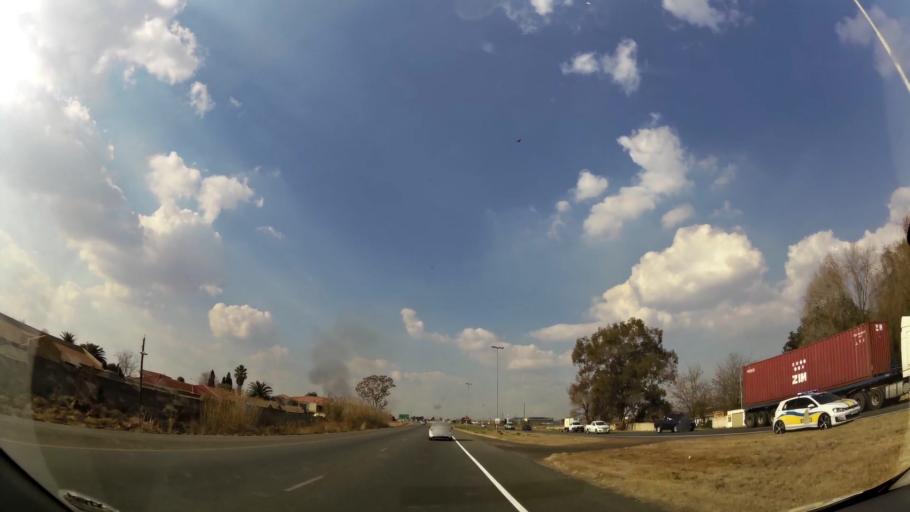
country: ZA
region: Gauteng
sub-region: Ekurhuleni Metropolitan Municipality
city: Boksburg
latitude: -26.2866
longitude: 28.2418
